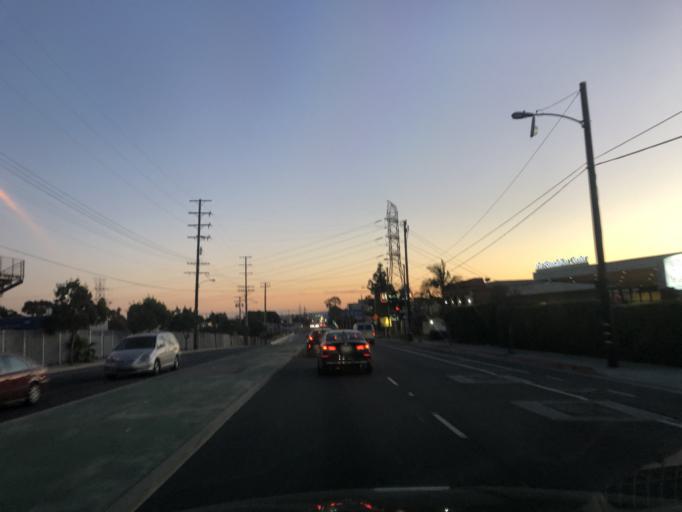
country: US
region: California
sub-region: Los Angeles County
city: West Athens
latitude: 33.9280
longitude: -118.3091
